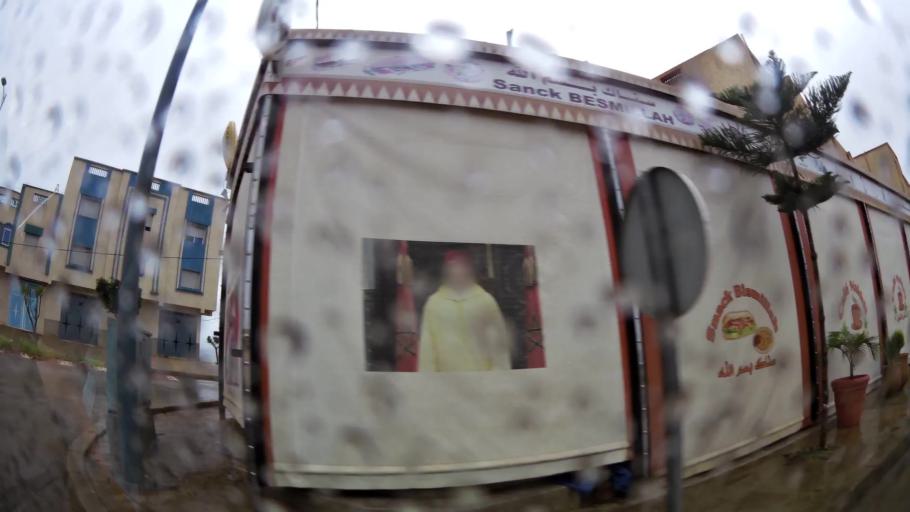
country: MA
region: Oriental
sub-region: Nador
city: Boudinar
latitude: 35.1110
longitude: -3.6423
